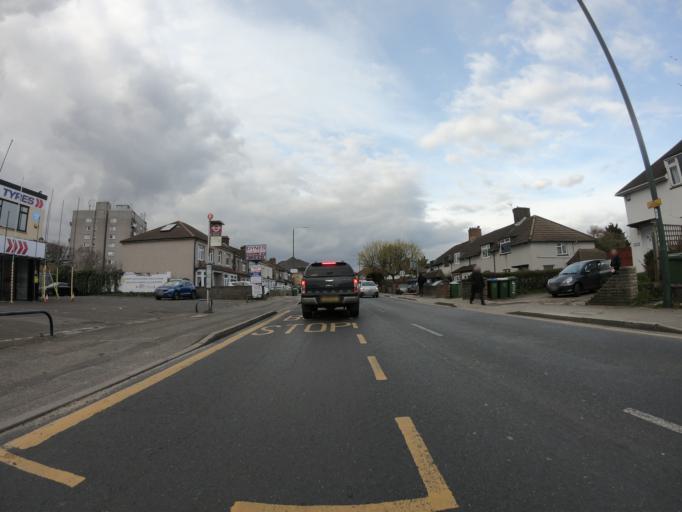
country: GB
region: England
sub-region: Greater London
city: Erith
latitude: 51.4702
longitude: 0.1602
